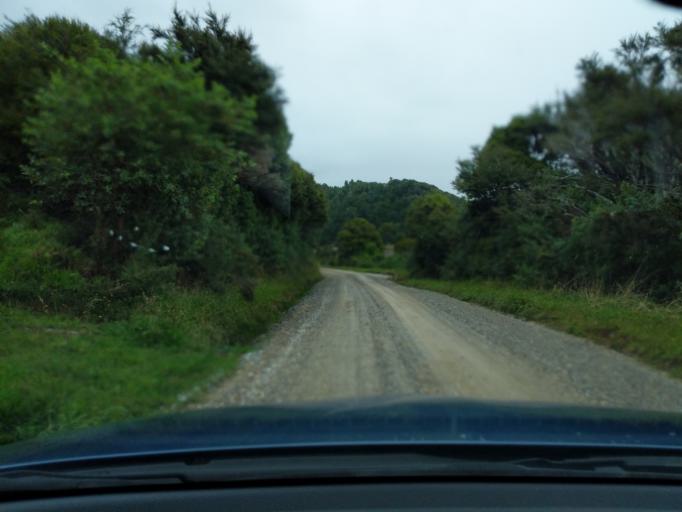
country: NZ
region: Tasman
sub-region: Tasman District
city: Takaka
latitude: -40.6264
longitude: 172.5163
